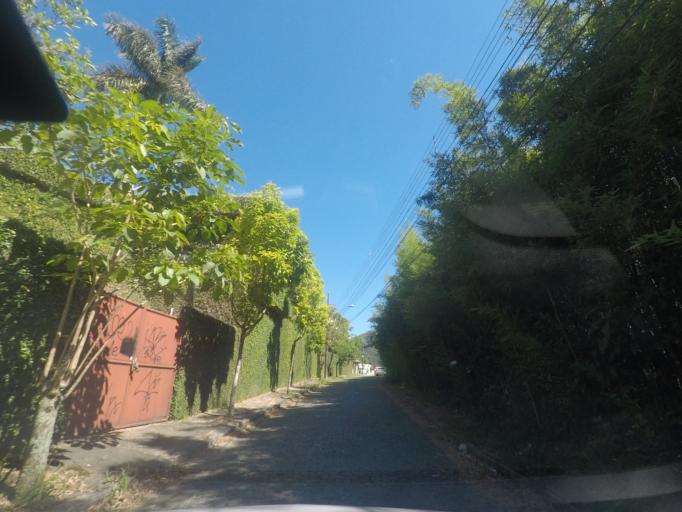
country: BR
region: Rio de Janeiro
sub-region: Petropolis
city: Petropolis
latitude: -22.5117
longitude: -43.1862
